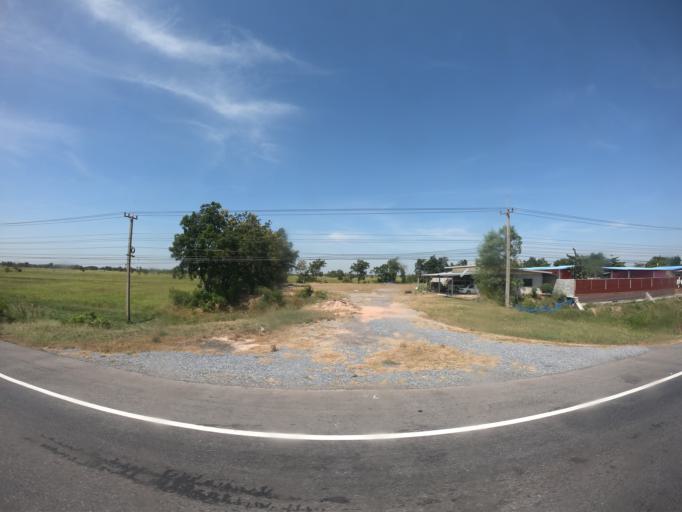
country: TH
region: Nakhon Ratchasima
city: Non Daeng
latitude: 15.4782
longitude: 102.5141
